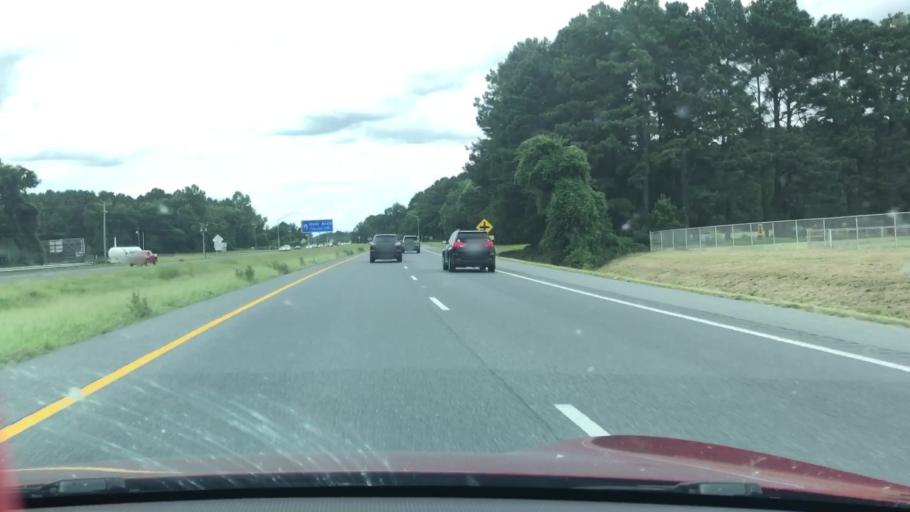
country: US
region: Maryland
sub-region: Somerset County
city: Princess Anne
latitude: 38.1953
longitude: -75.6965
